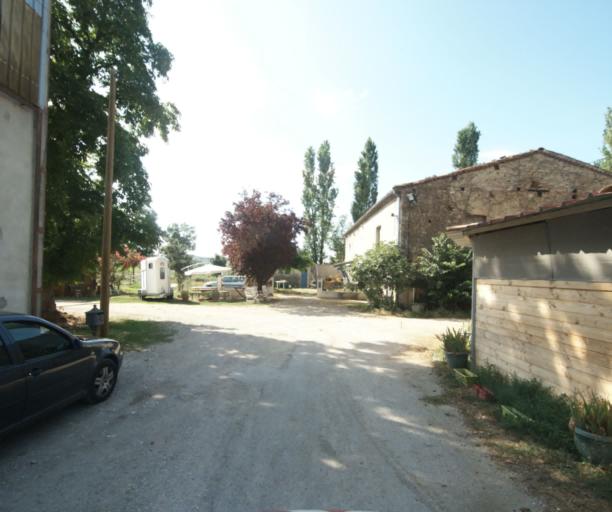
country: FR
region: Midi-Pyrenees
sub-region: Departement du Tarn
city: Puylaurens
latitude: 43.5215
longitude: 1.9669
